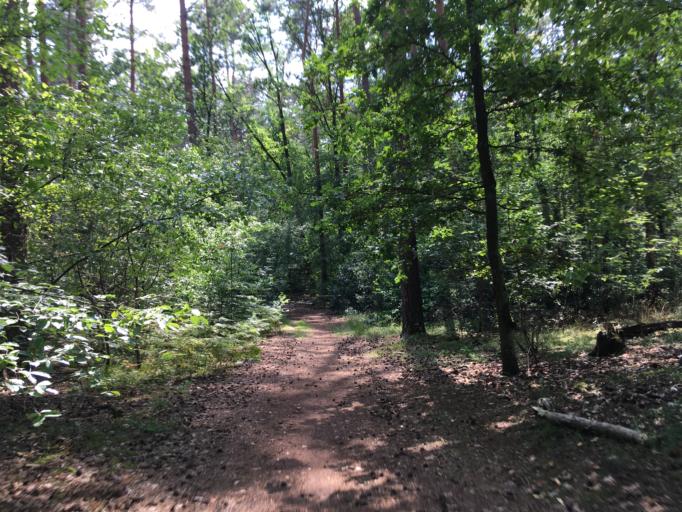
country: DE
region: Brandenburg
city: Glienicke
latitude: 52.6761
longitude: 13.3324
